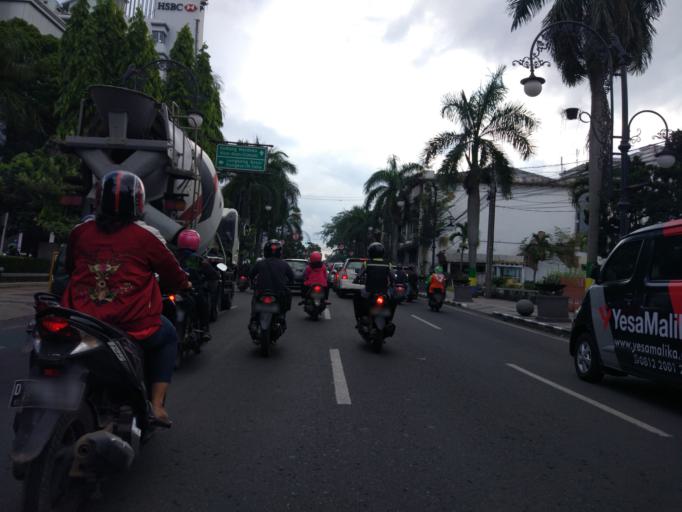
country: ID
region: West Java
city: Bandung
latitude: -6.9219
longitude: 107.6132
